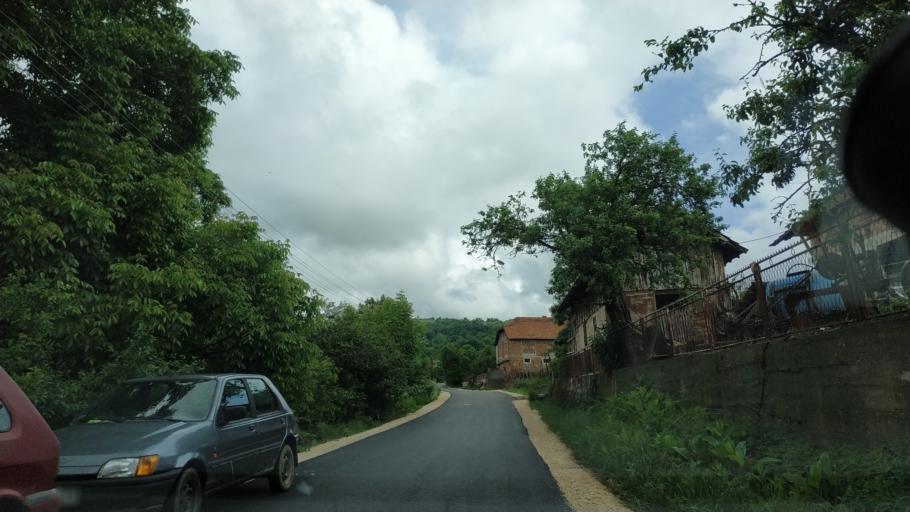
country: RS
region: Central Serbia
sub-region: Zajecarski Okrug
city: Soko Banja
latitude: 43.6757
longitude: 21.9143
